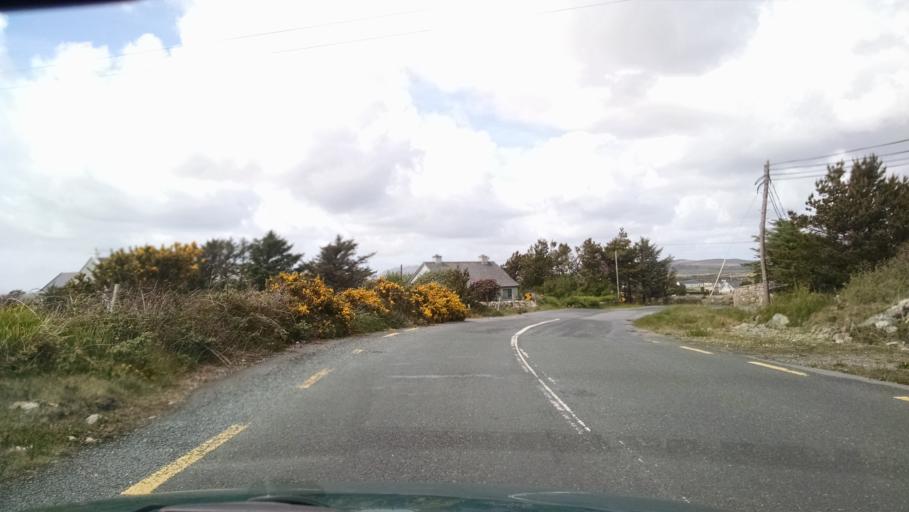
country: IE
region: Connaught
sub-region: County Galway
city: Clifden
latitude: 53.3156
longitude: -9.8043
